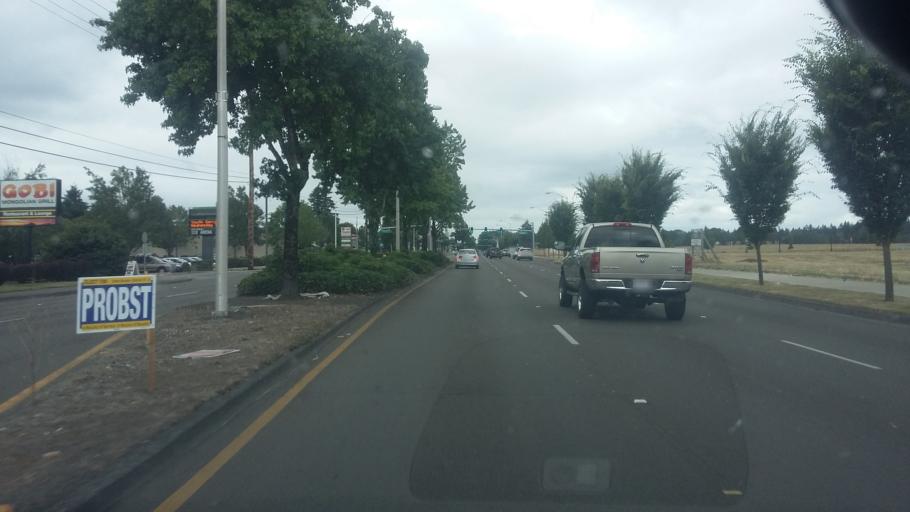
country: US
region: Washington
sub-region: Clark County
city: Mill Plain
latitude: 45.6178
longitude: -122.5241
